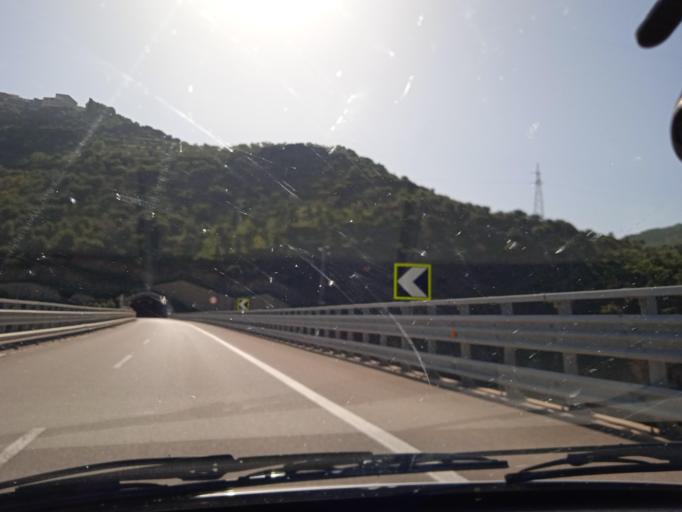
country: IT
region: Sicily
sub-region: Messina
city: Caronia
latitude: 38.0189
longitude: 14.4354
